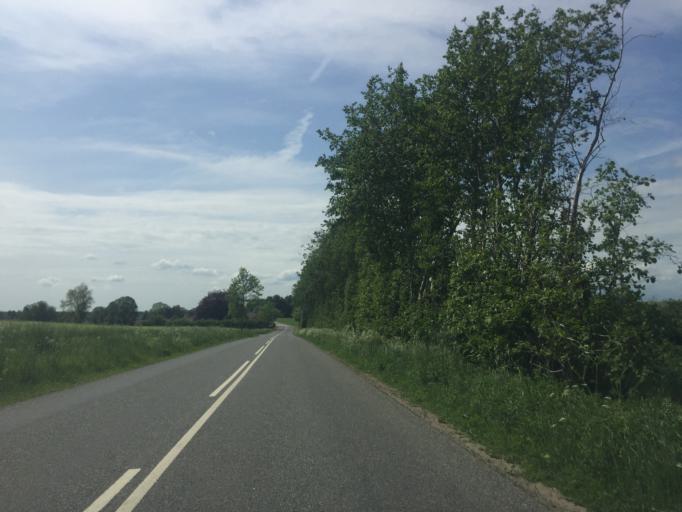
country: DK
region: South Denmark
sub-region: Svendborg Kommune
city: Thuro By
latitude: 55.1440
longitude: 10.6888
